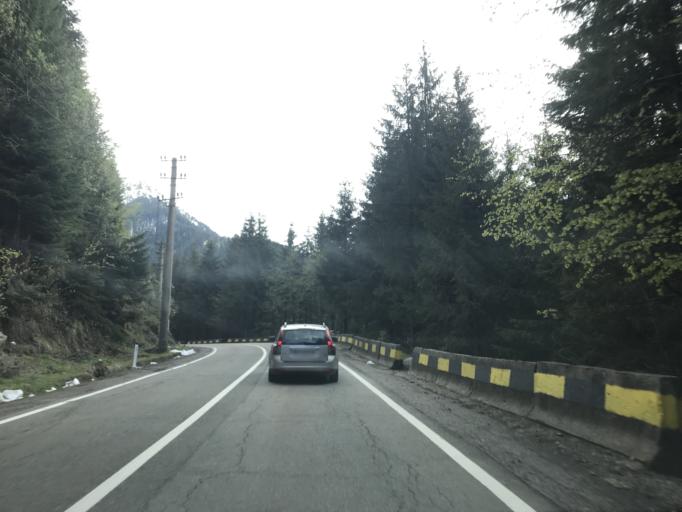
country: RO
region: Sibiu
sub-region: Comuna Cartisoara
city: Cartisoara
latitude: 45.6480
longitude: 24.6054
